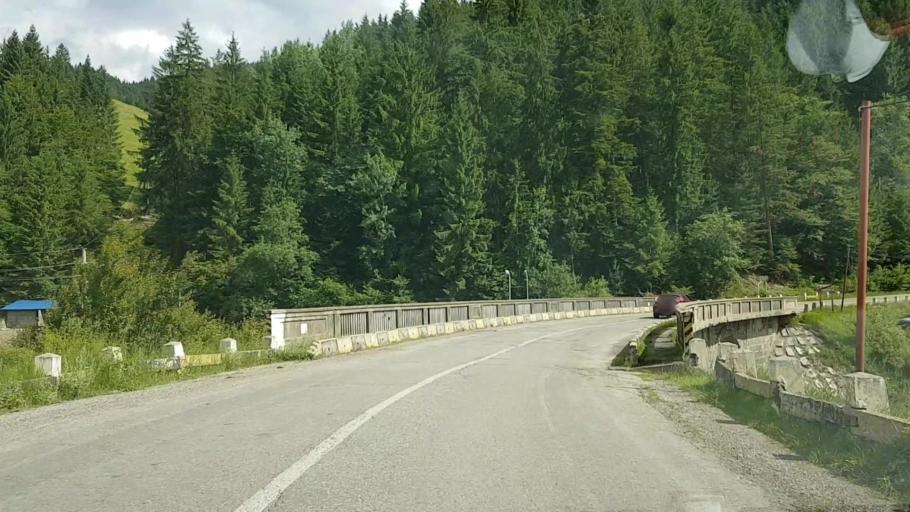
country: RO
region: Neamt
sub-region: Comuna Hangu
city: Hangu
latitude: 47.0181
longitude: 26.0868
